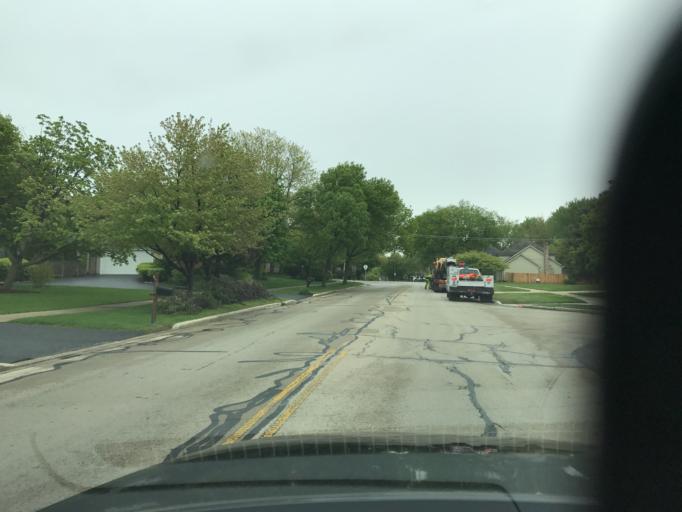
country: US
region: Illinois
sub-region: DuPage County
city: Naperville
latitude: 41.7630
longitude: -88.1224
